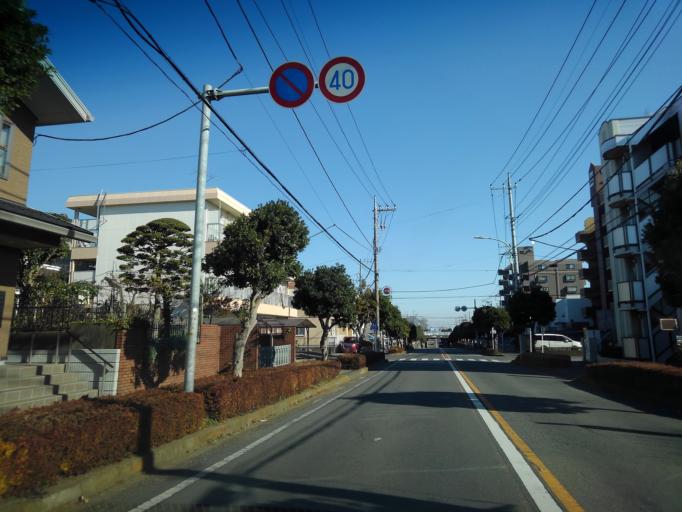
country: JP
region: Saitama
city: Tokorozawa
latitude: 35.7994
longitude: 139.5189
